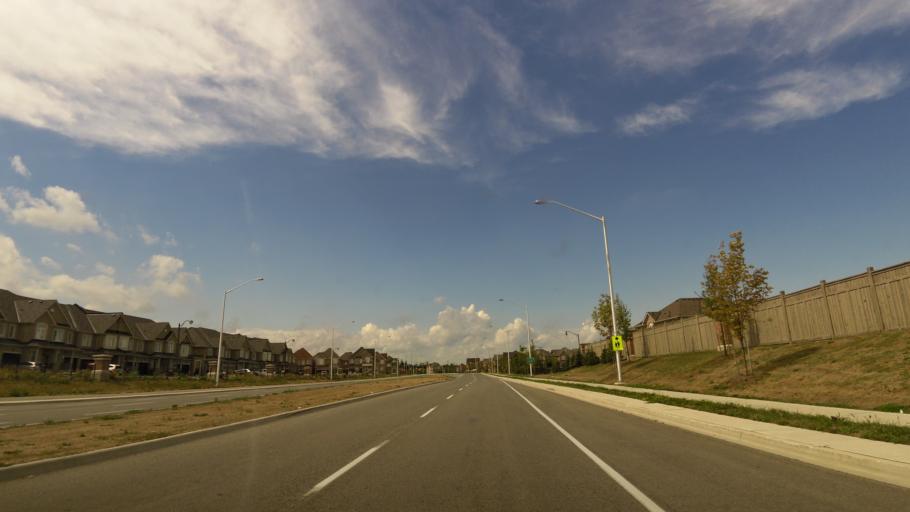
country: CA
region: Ontario
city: Brampton
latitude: 43.7674
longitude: -79.7192
